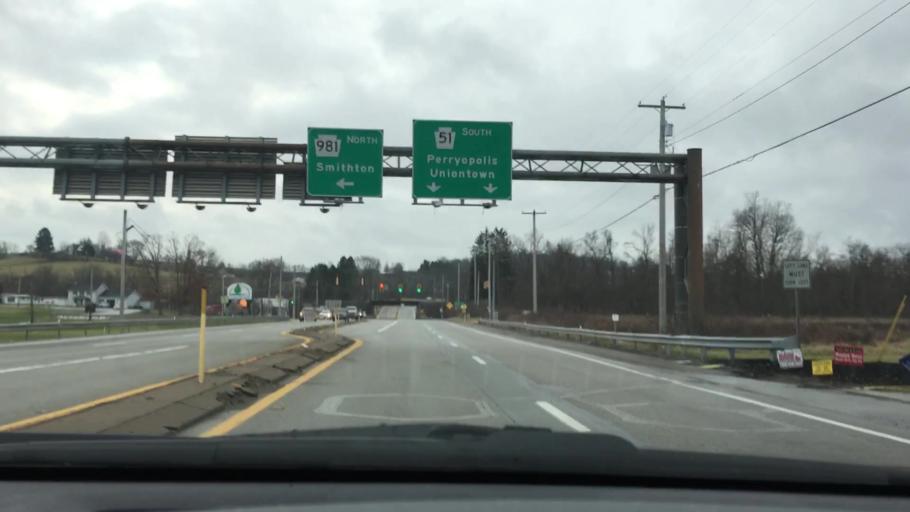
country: US
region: Pennsylvania
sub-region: Westmoreland County
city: West Newton
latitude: 40.1525
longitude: -79.7746
